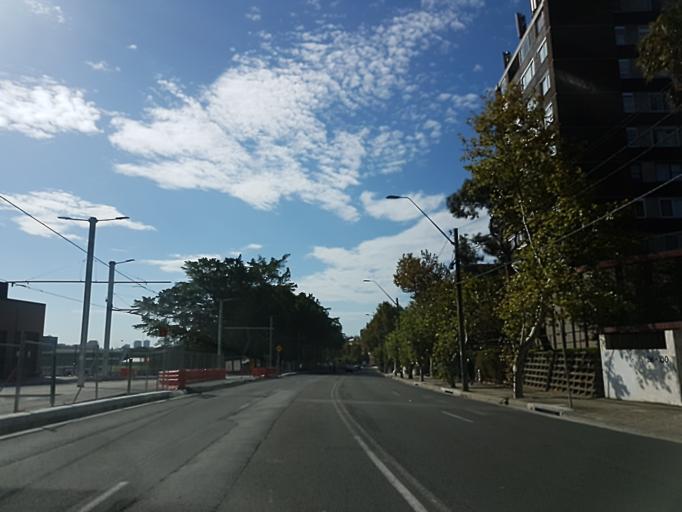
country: AU
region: New South Wales
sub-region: Randwick
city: Randwick
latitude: -33.9103
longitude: 151.2352
